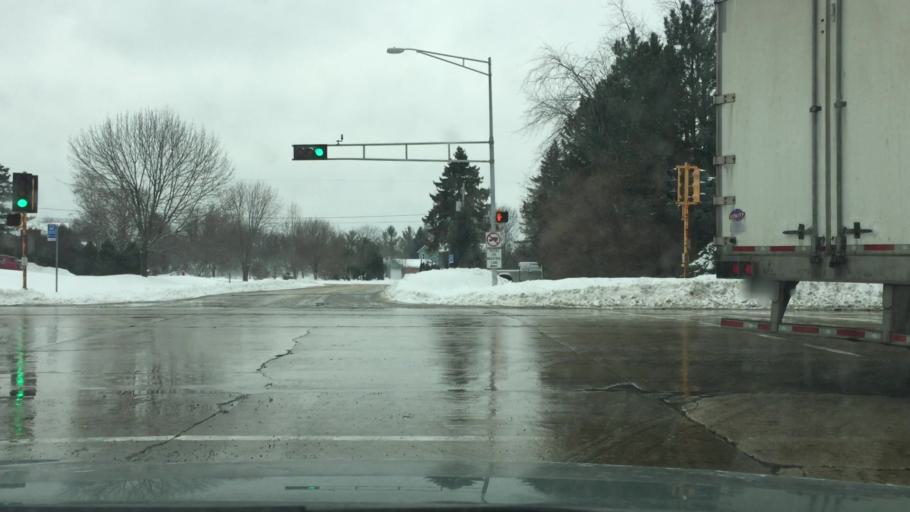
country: US
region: Wisconsin
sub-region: Waukesha County
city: Waukesha
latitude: 42.9883
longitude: -88.2433
